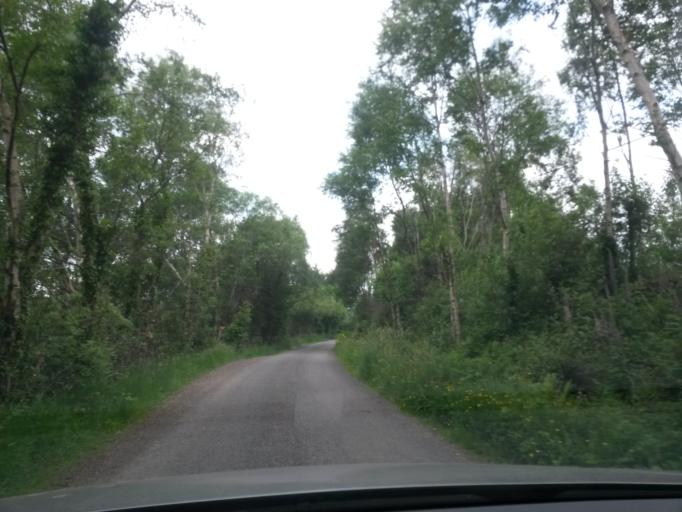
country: IE
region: Munster
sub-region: Ciarrai
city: Kenmare
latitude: 51.8716
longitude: -9.5361
